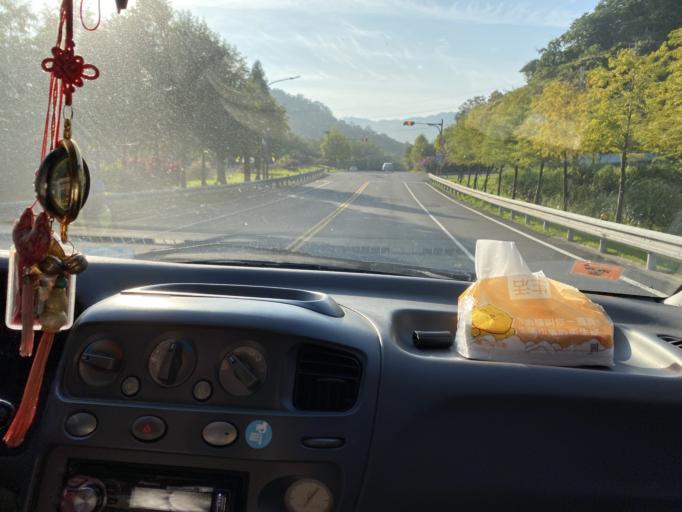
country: TW
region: Taiwan
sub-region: Keelung
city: Keelung
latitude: 25.0518
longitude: 121.7733
